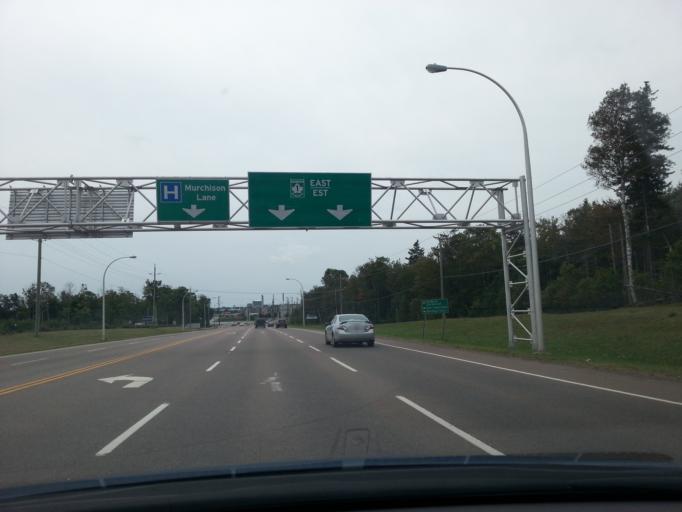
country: CA
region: Prince Edward Island
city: Charlottetown
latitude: 46.2562
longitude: -63.1021
